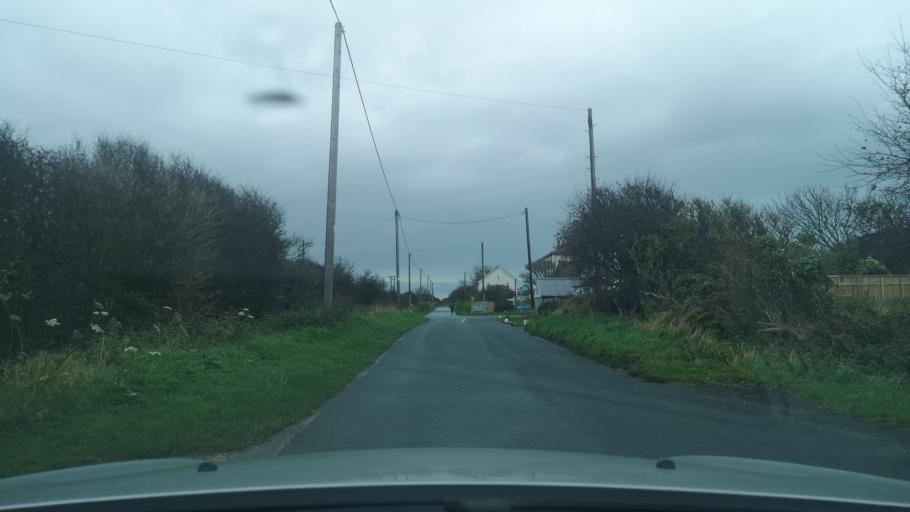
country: GB
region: England
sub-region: East Riding of Yorkshire
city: Easington
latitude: 53.6195
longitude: 0.1395
